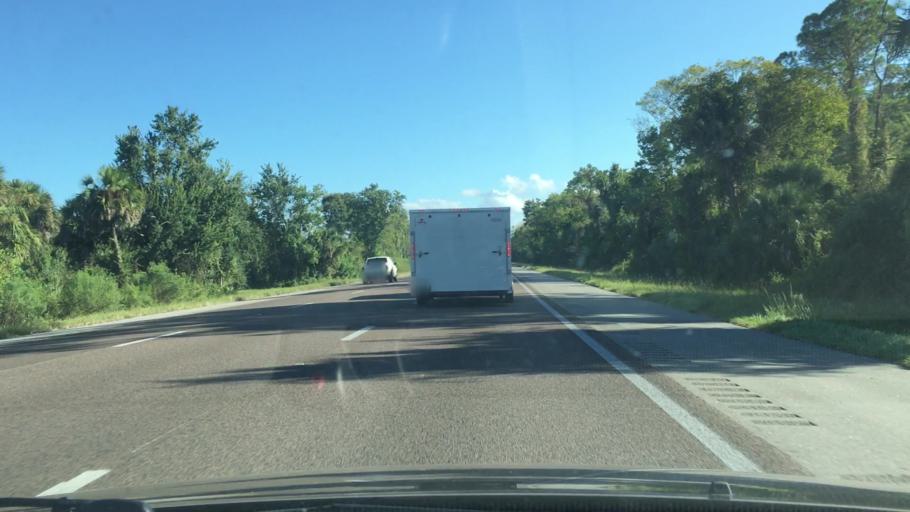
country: US
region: Florida
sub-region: Volusia County
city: Oak Hill
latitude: 28.8599
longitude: -80.9182
